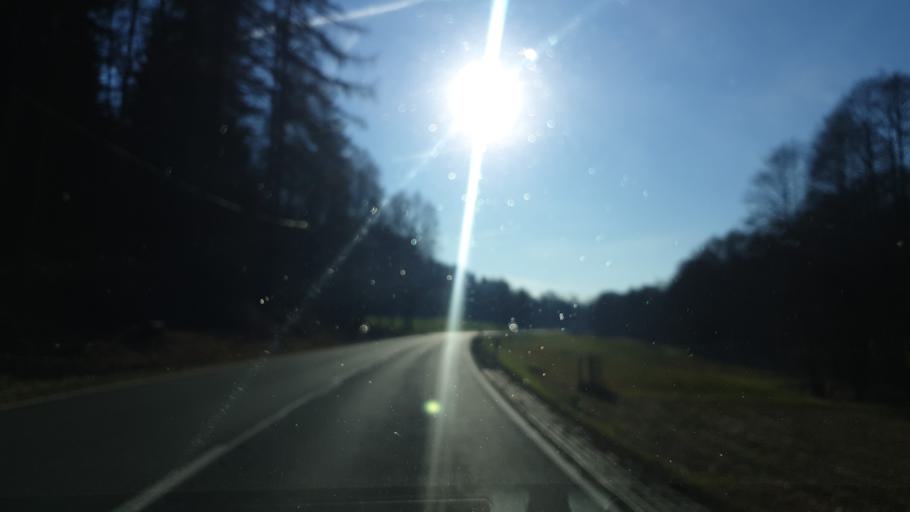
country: DE
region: Saxony
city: Bad Brambach
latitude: 50.2651
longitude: 12.3009
